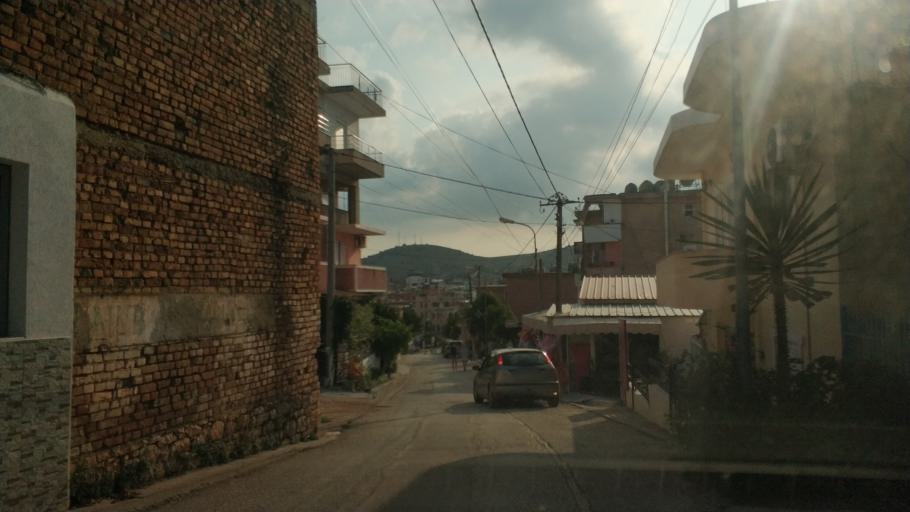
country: AL
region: Vlore
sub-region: Rrethi i Sarandes
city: Xarre
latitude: 39.7691
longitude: 20.0004
